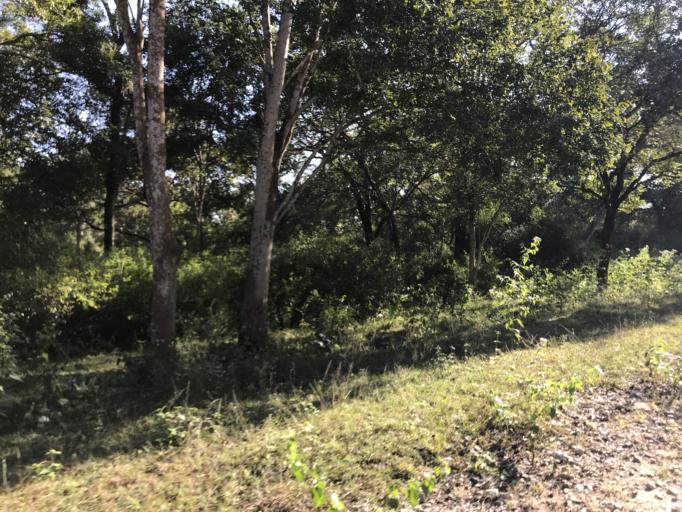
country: IN
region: Karnataka
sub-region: Mysore
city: Heggadadevankote
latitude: 11.9622
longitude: 76.2401
